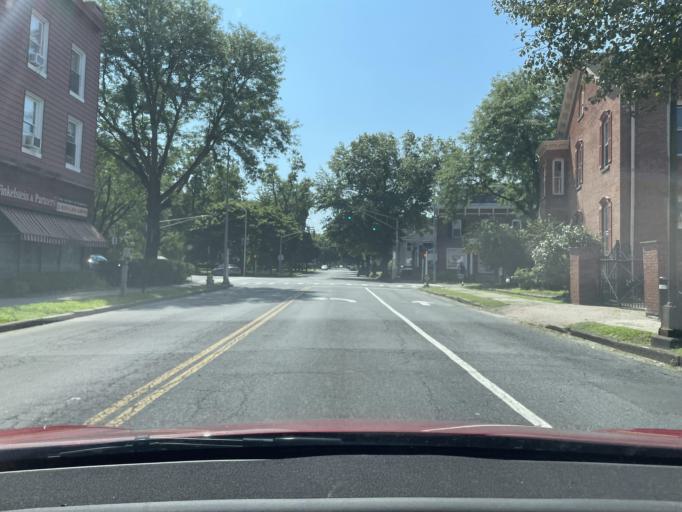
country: US
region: New York
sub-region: Ulster County
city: Kingston
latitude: 41.9330
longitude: -74.0160
